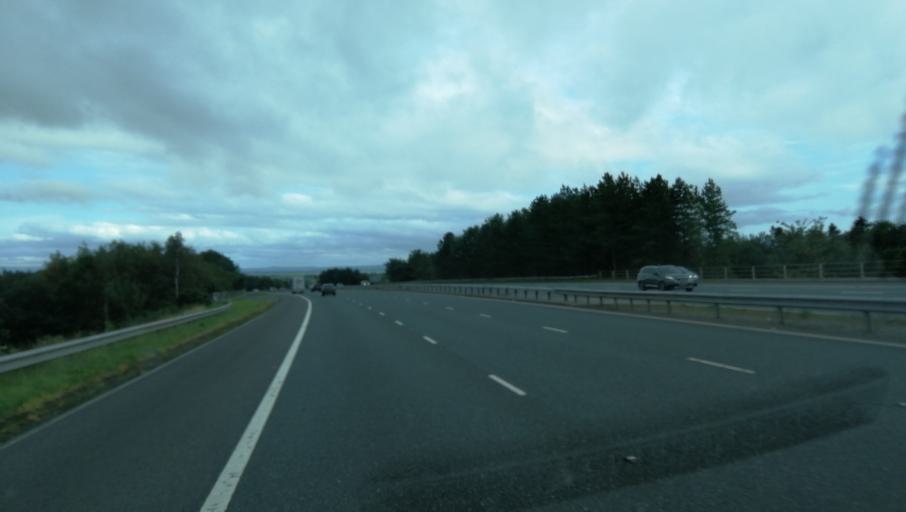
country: GB
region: Scotland
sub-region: Dumfries and Galloway
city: Gretna
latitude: 55.0207
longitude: -3.1224
